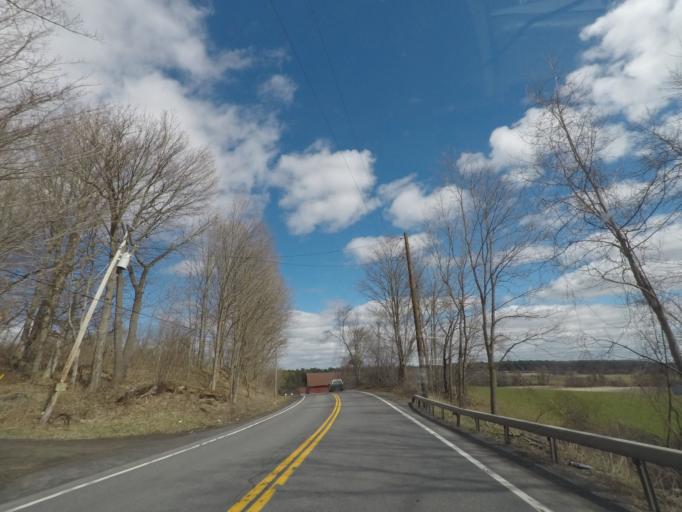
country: US
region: New York
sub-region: Albany County
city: Voorheesville
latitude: 42.5682
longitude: -73.9052
